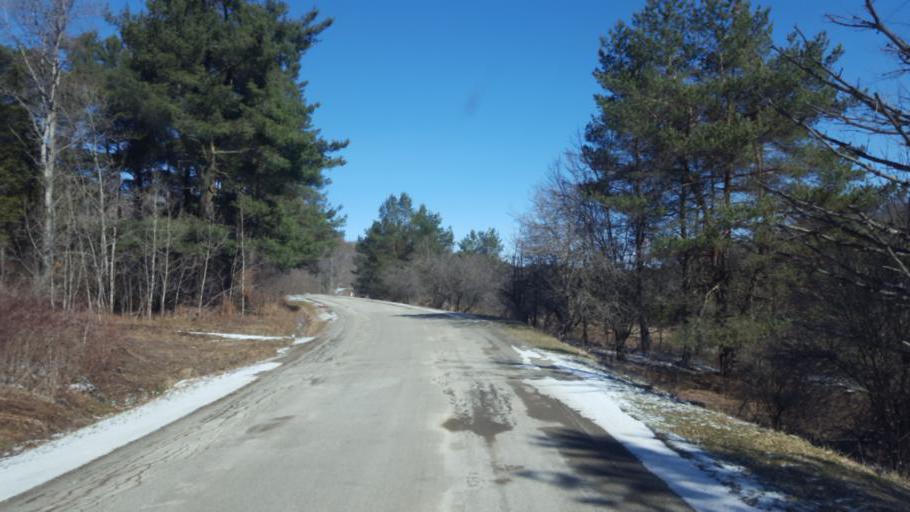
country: US
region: New York
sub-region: Allegany County
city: Wellsville
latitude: 42.0552
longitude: -77.9543
